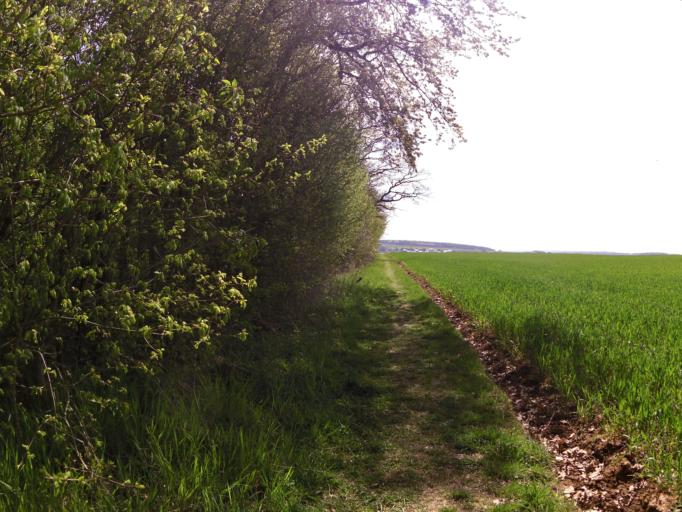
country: DE
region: Bavaria
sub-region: Regierungsbezirk Unterfranken
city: Rimpar
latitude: 49.8601
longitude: 9.9785
